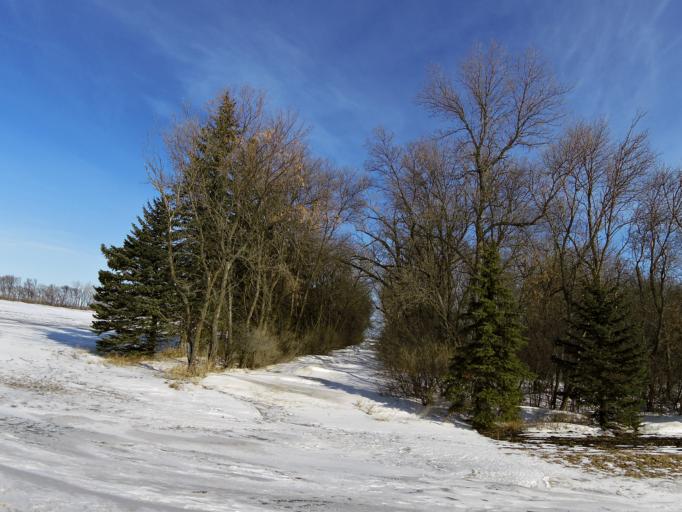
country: US
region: North Dakota
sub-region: Walsh County
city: Grafton
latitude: 48.4063
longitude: -97.2120
